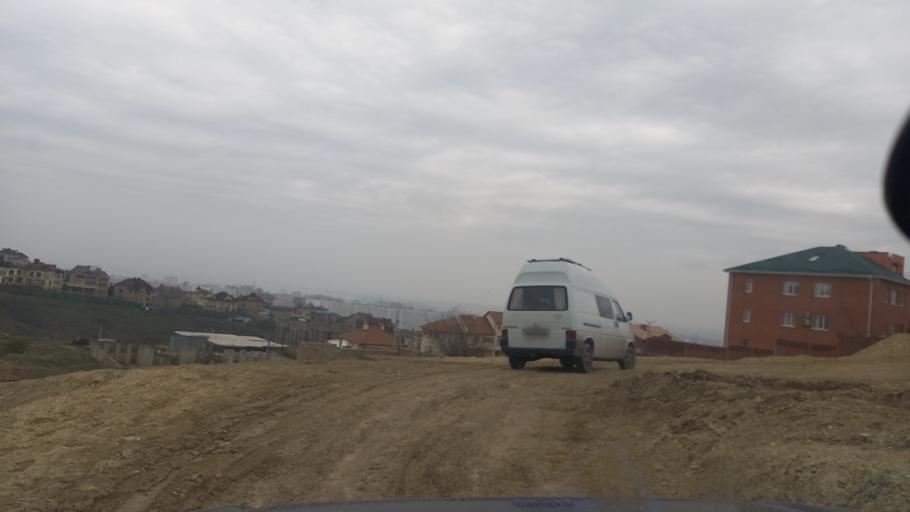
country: RU
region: Krasnodarskiy
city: Anapa
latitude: 44.8553
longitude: 37.3405
